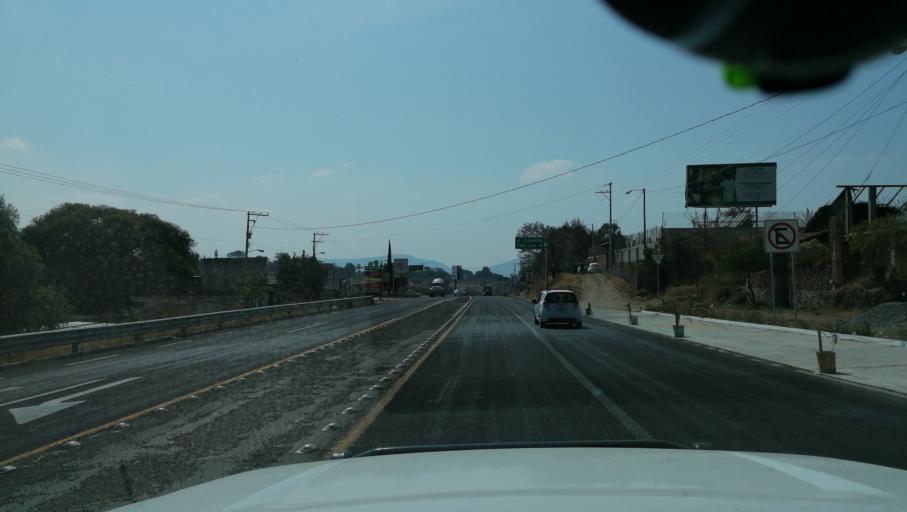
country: MX
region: Puebla
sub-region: Atlixco
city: San Agustin Huixaxtla
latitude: 18.9235
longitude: -98.4108
